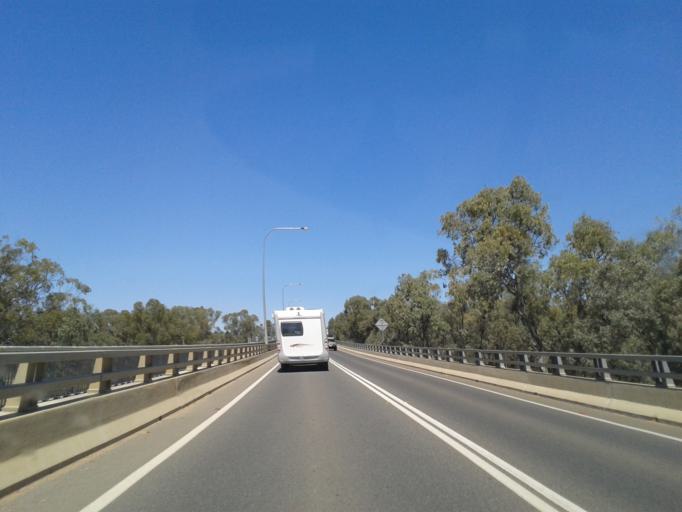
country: AU
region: Victoria
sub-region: Mildura Shire
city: Ouyen
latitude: -34.5742
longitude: 142.7659
